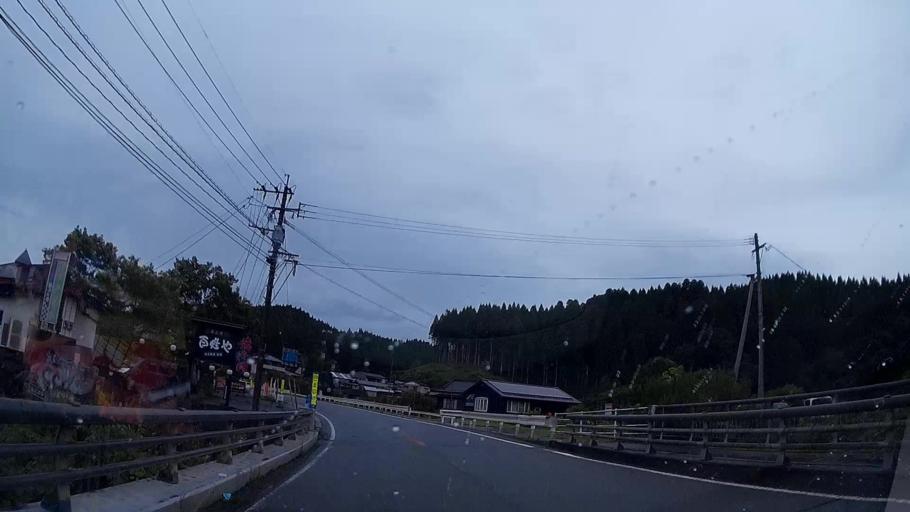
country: JP
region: Oita
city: Tsukawaki
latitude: 33.1256
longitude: 131.0640
